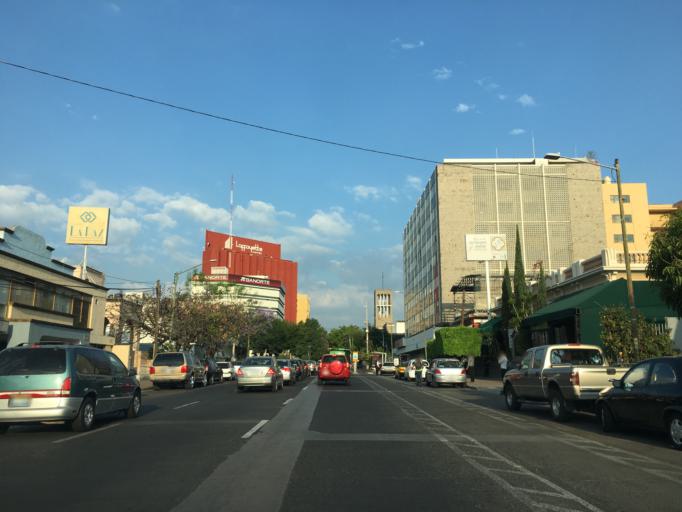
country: MX
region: Jalisco
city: Guadalajara
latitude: 20.6723
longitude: -103.3674
